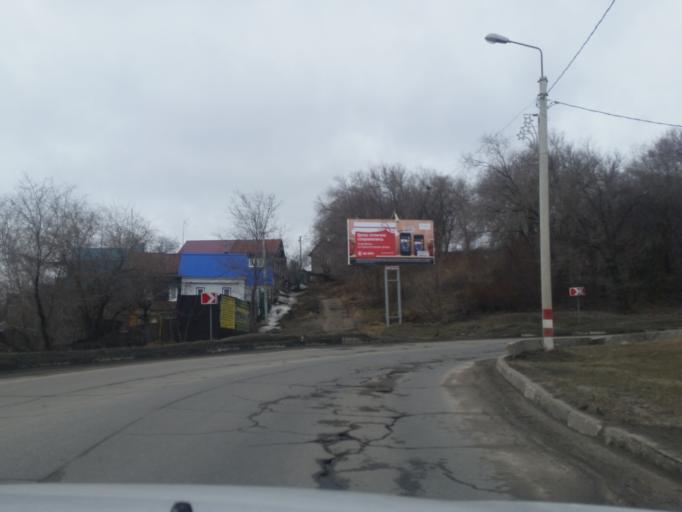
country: RU
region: Ulyanovsk
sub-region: Ulyanovskiy Rayon
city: Ulyanovsk
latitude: 54.3092
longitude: 48.4072
